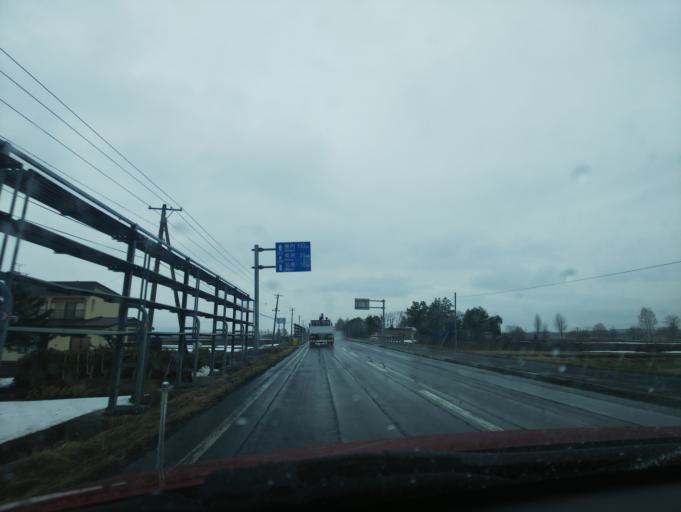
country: JP
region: Hokkaido
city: Nayoro
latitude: 44.2168
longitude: 142.3948
